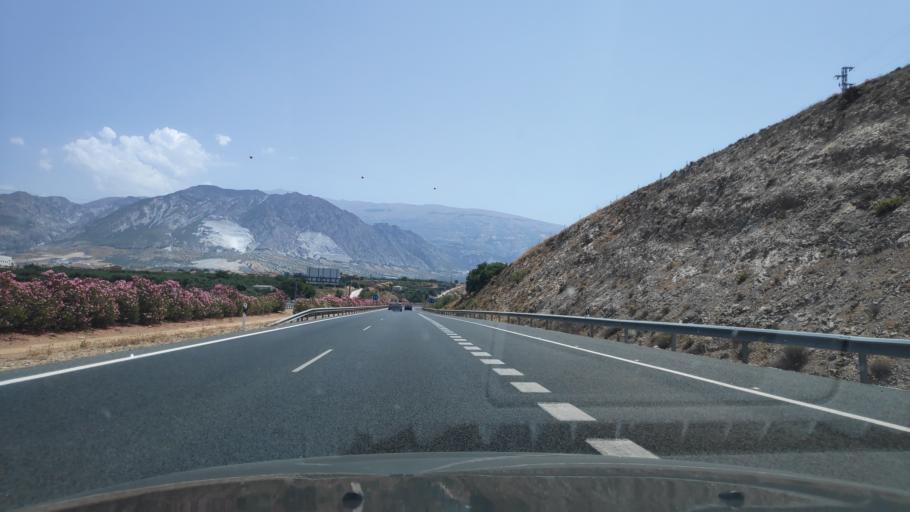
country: ES
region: Andalusia
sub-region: Provincia de Granada
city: Durcal
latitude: 36.9877
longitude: -3.6008
